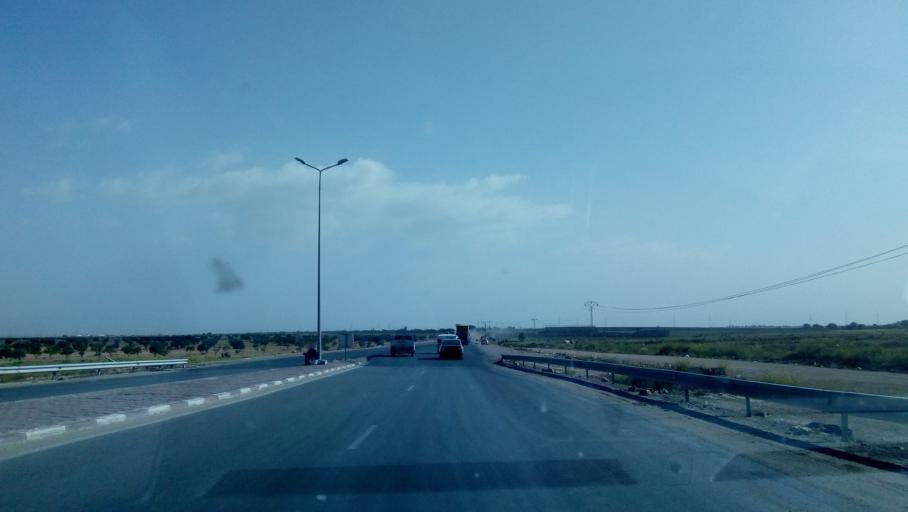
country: TN
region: Qabis
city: Gabes
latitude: 33.8817
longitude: 10.0066
